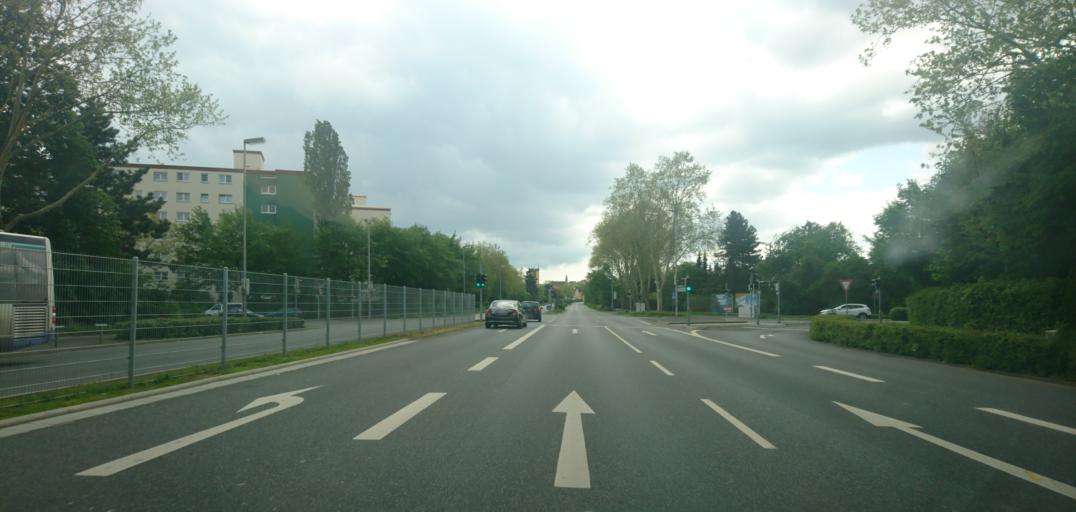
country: DE
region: Hesse
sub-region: Regierungsbezirk Darmstadt
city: Dietzenbach
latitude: 50.0153
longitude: 8.7793
